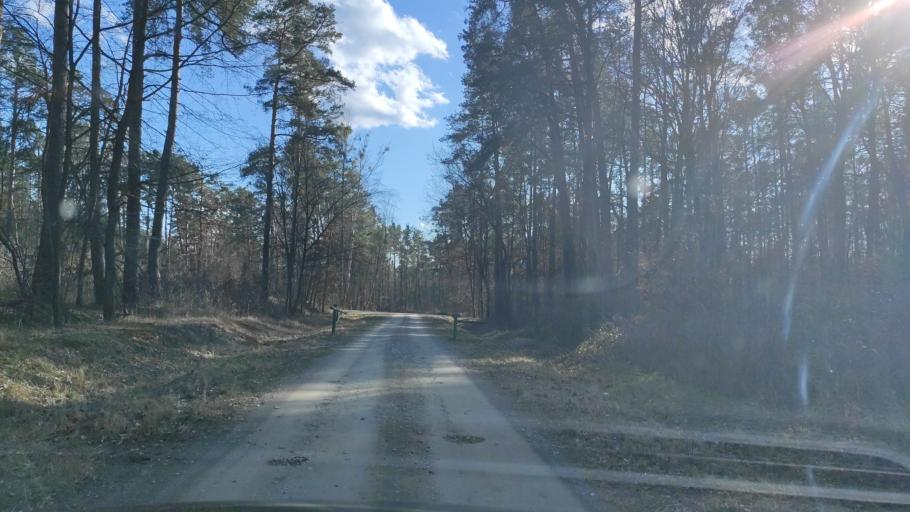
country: PL
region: Masovian Voivodeship
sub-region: Powiat radomski
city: Jedlnia-Letnisko
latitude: 51.4441
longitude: 21.2932
